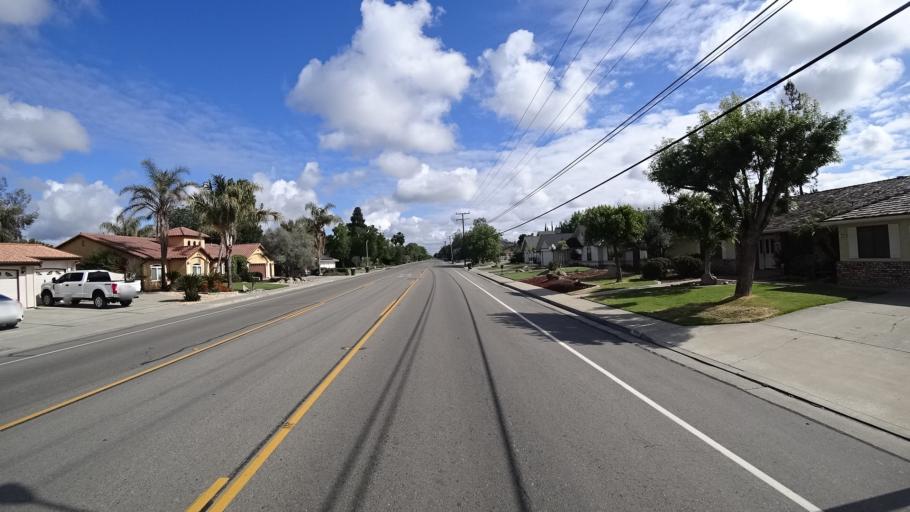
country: US
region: California
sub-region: Kings County
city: Lucerne
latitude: 36.3587
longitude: -119.6460
